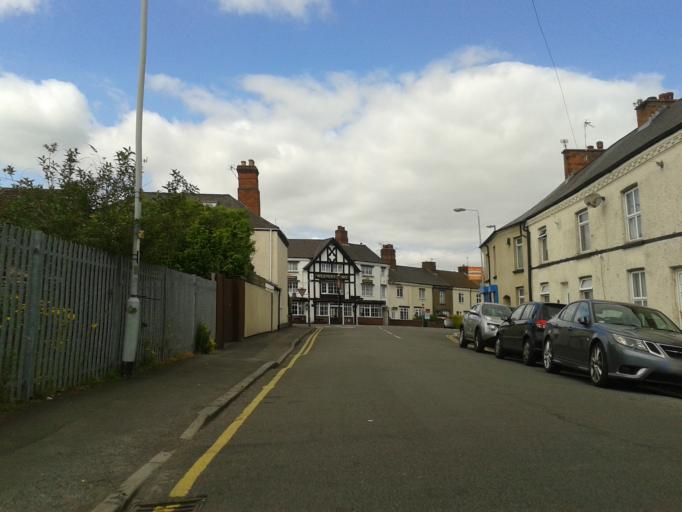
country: GB
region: England
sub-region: Leicestershire
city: Hinckley
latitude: 52.5464
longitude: -1.3669
